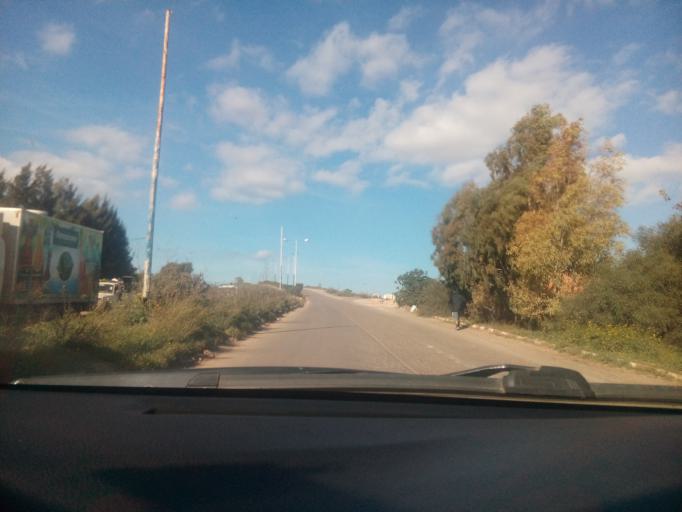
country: DZ
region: Oran
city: Bir el Djir
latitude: 35.6812
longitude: -0.5689
